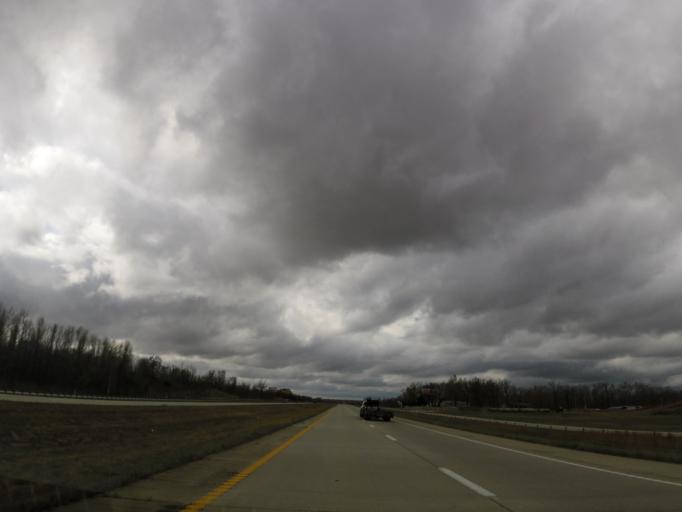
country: US
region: Missouri
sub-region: Butler County
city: Poplar Bluff
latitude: 36.7103
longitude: -90.4695
